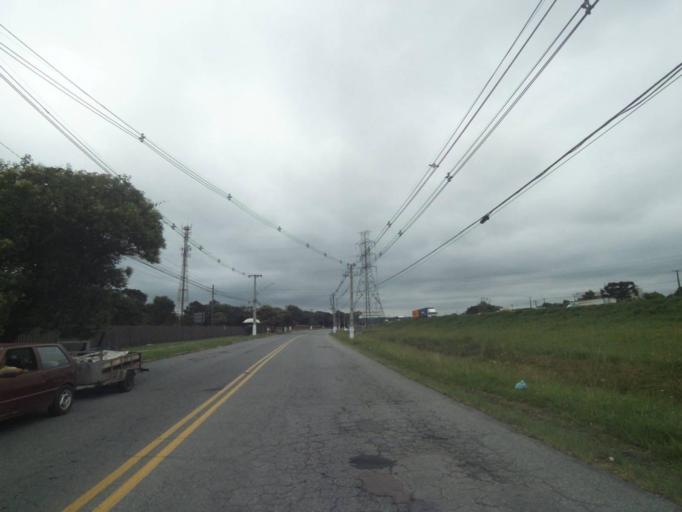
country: BR
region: Parana
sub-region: Araucaria
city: Araucaria
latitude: -25.5304
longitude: -49.3263
